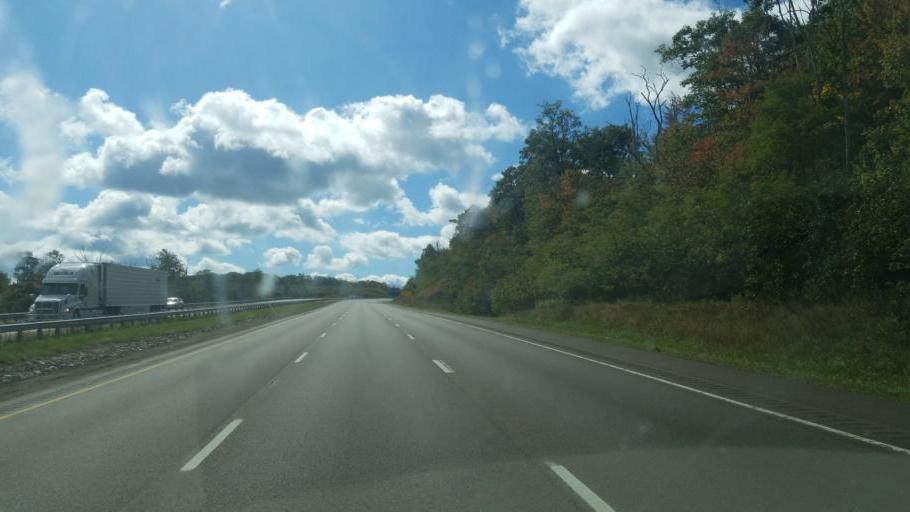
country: US
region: Pennsylvania
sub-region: Somerset County
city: Meyersdale
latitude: 39.6831
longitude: -79.2096
